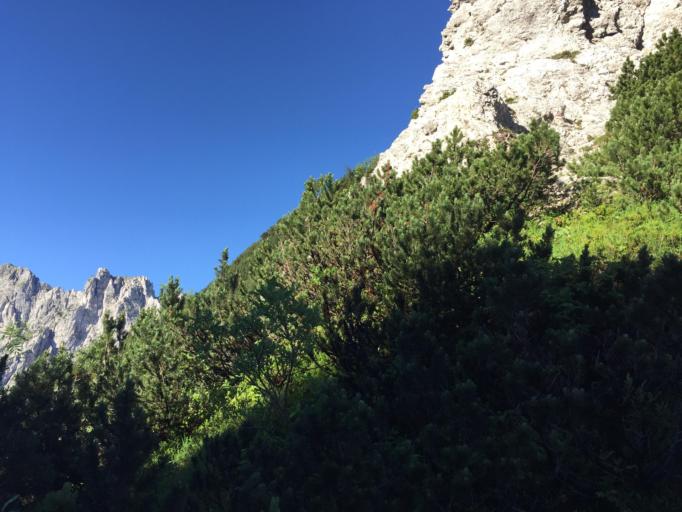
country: IT
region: Friuli Venezia Giulia
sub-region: Provincia di Udine
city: Pontebba
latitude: 46.4722
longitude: 13.2567
